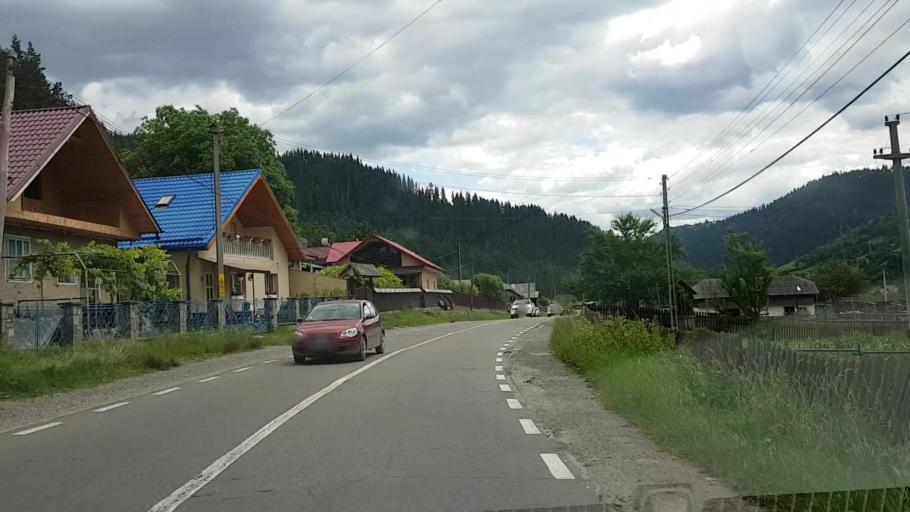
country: RO
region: Neamt
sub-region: Comuna Poiana Teiului
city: Poiana Teiului
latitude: 47.1308
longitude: 25.9002
